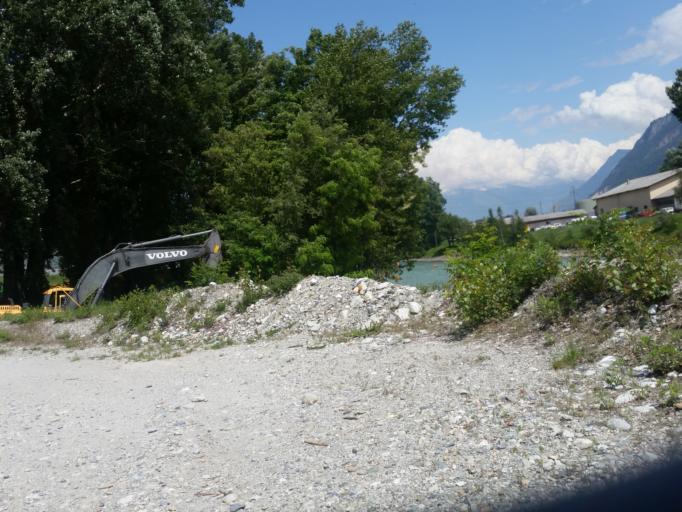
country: CH
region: Valais
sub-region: Sion District
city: Sitten
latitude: 46.2224
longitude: 7.3618
